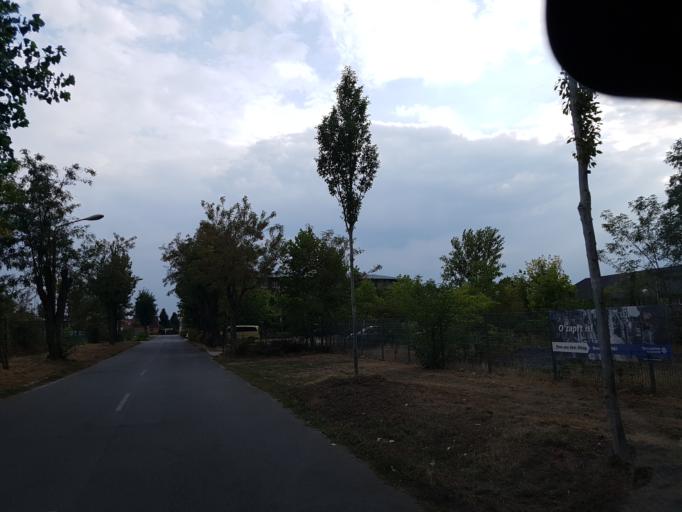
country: DE
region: Saxony-Anhalt
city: Abtsdorf
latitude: 51.8659
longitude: 12.6865
